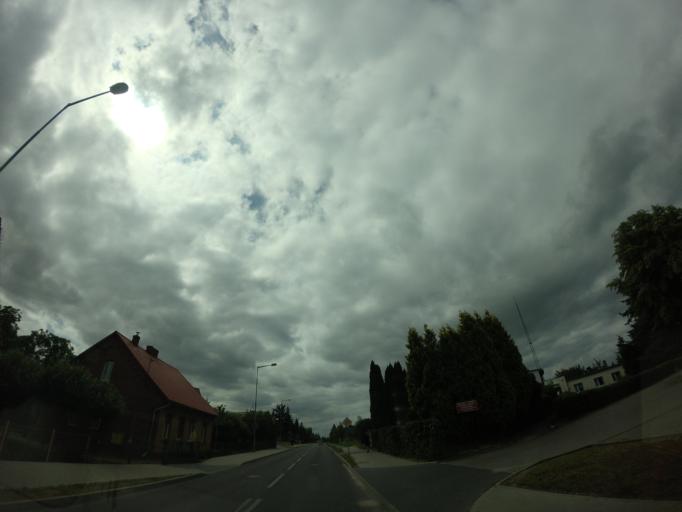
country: PL
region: Lubusz
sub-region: Powiat strzelecko-drezdenecki
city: Strzelce Krajenskie
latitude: 52.8729
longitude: 15.5297
